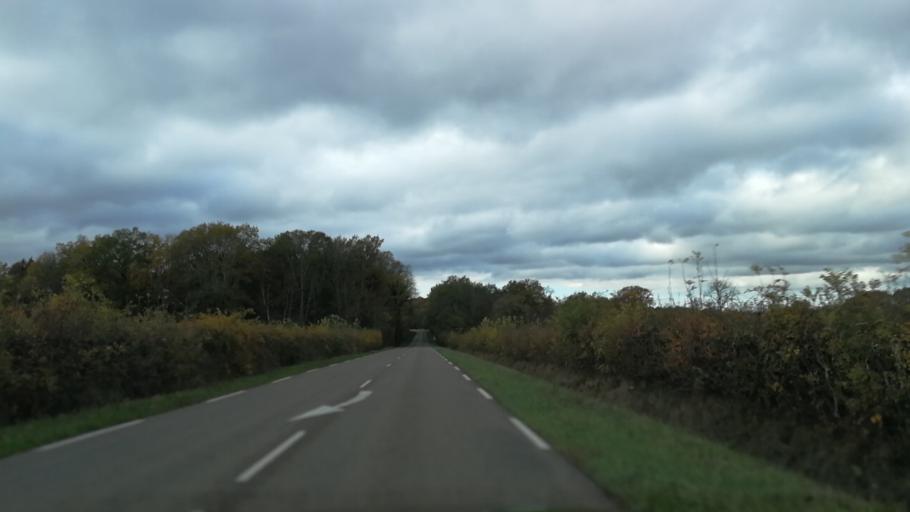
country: FR
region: Bourgogne
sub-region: Departement de la Cote-d'Or
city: Saulieu
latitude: 47.2579
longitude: 4.3260
